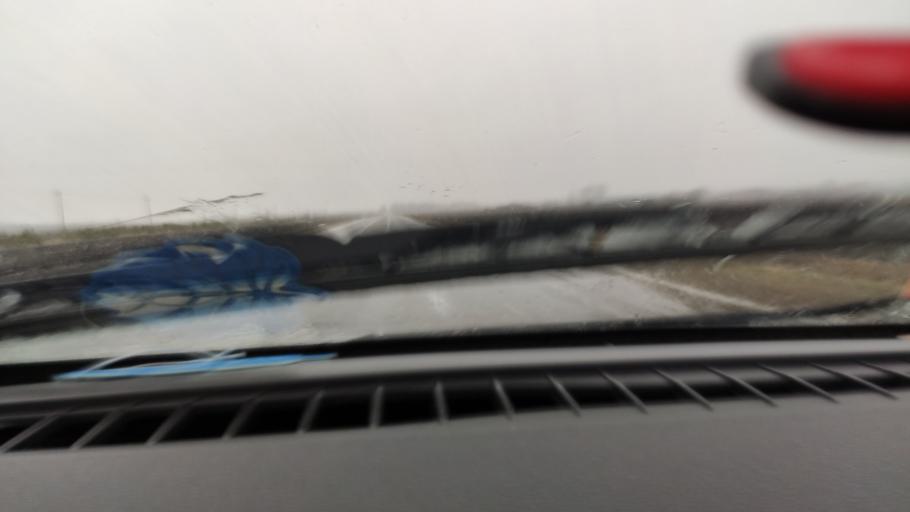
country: RU
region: Tatarstan
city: Cheremshan
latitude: 54.7149
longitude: 51.2078
